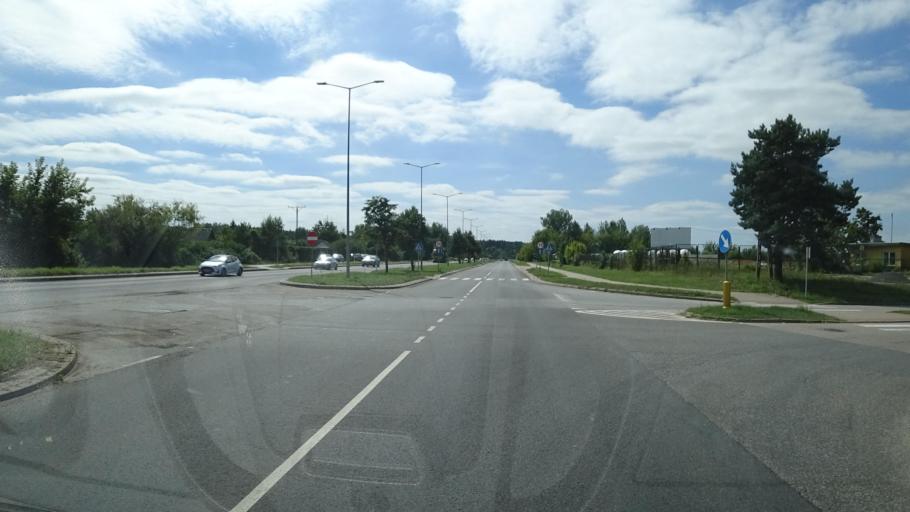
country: PL
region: Warmian-Masurian Voivodeship
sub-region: Powiat elcki
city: Elk
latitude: 53.8262
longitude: 22.3911
